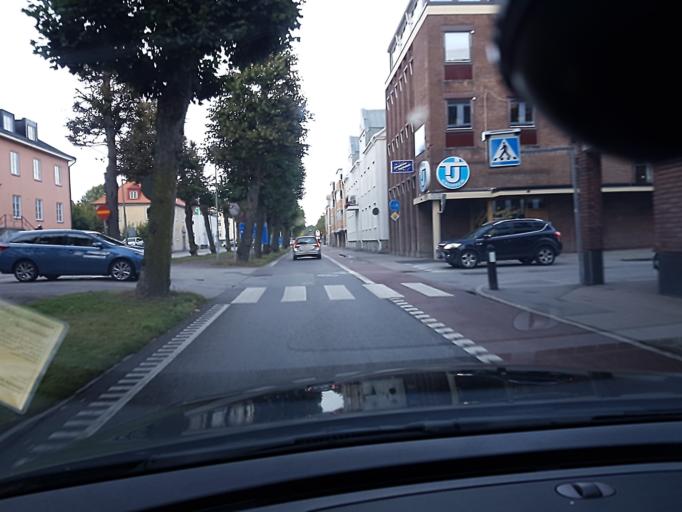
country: SE
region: Kronoberg
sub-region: Vaxjo Kommun
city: Vaexjoe
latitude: 56.8799
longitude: 14.8117
